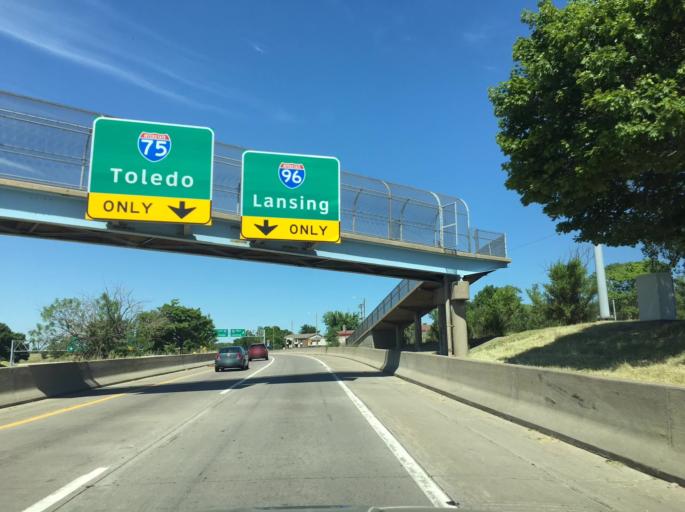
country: US
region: Michigan
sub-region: Wayne County
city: Detroit
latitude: 42.3331
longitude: -83.0805
